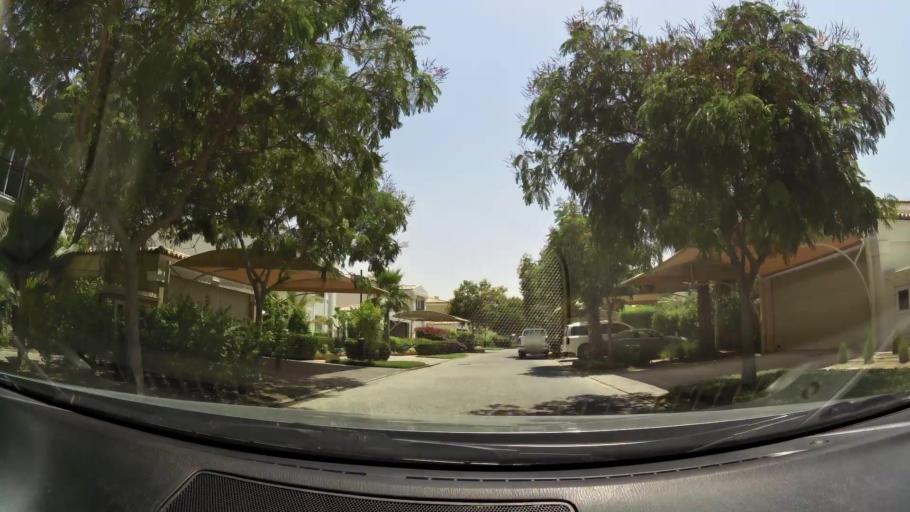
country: AE
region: Dubai
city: Dubai
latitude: 24.9969
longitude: 55.1661
